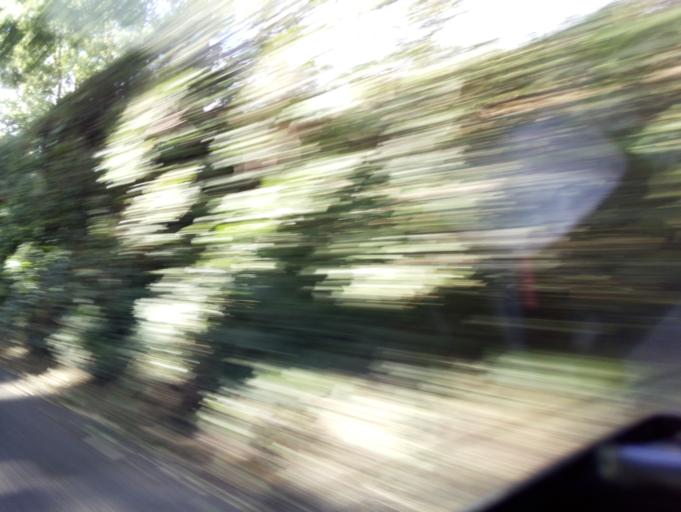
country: GB
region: England
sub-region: Devon
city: Newton Poppleford
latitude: 50.7009
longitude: -3.2814
